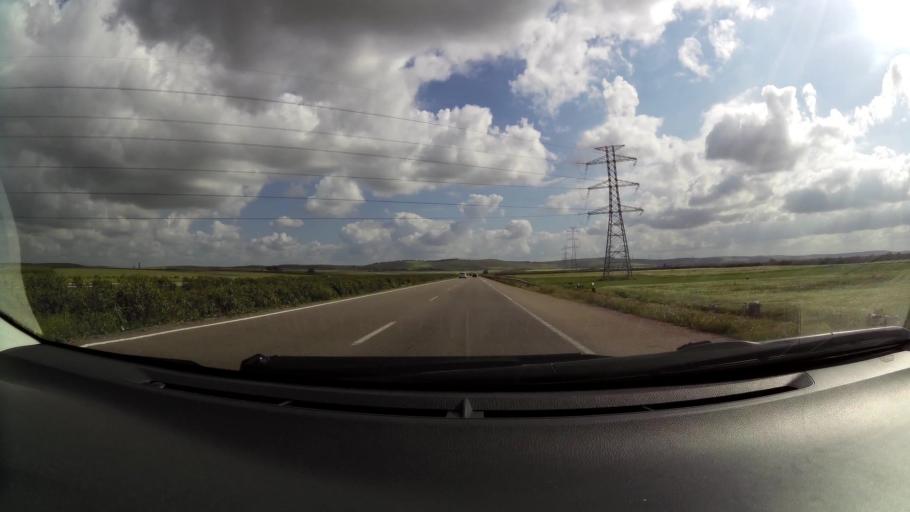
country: MA
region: Chaouia-Ouardigha
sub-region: Settat Province
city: Settat
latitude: 33.1105
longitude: -7.5820
